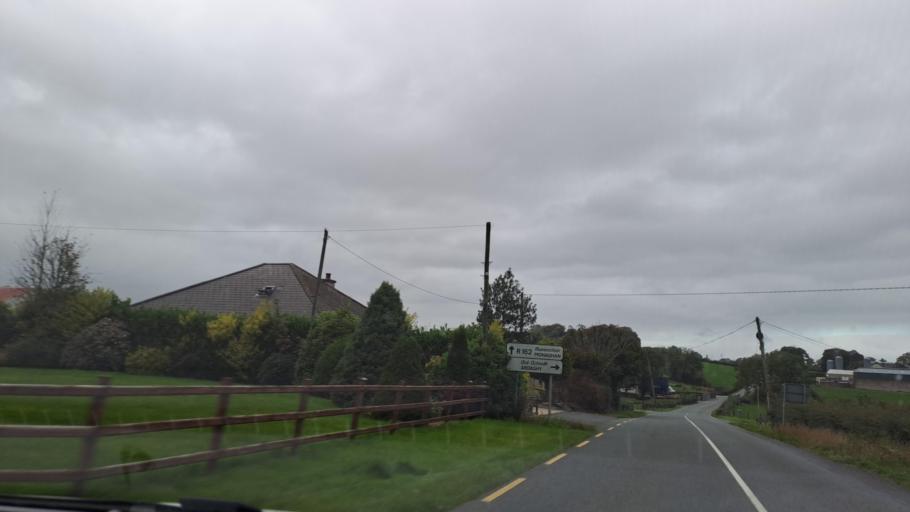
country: IE
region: Ulster
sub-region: County Monaghan
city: Monaghan
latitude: 54.1892
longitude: -6.9370
